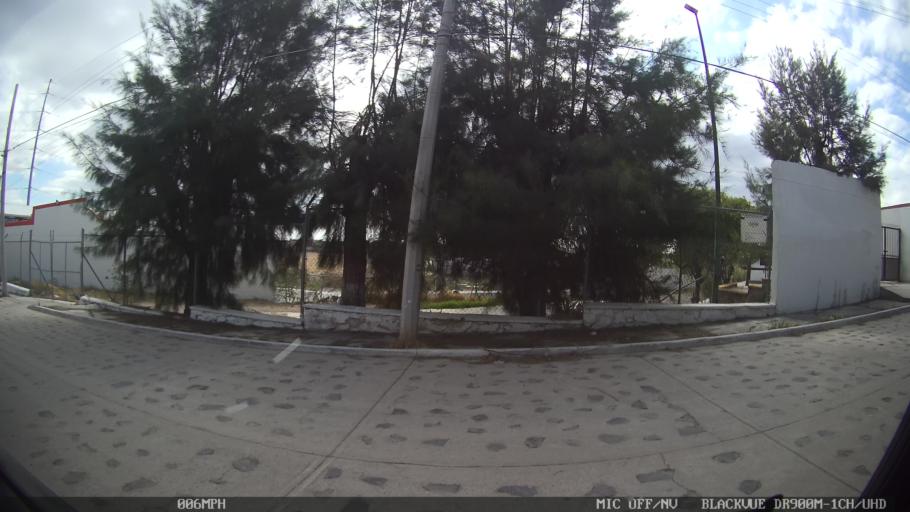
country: MX
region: Jalisco
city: Tlaquepaque
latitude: 20.6852
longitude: -103.2568
